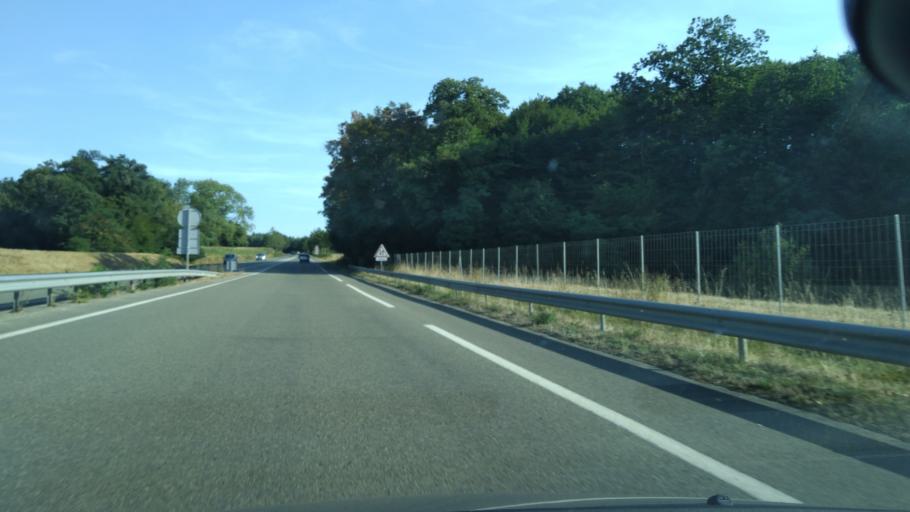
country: FR
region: Pays de la Loire
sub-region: Departement de la Mayenne
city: Entrammes
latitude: 47.9978
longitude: -0.7216
